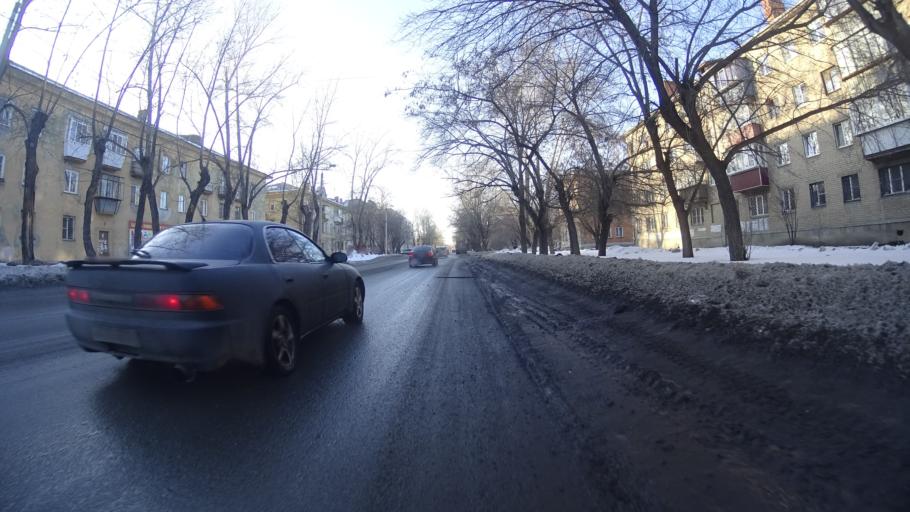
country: RU
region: Chelyabinsk
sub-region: Gorod Chelyabinsk
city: Chelyabinsk
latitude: 55.1279
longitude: 61.4696
